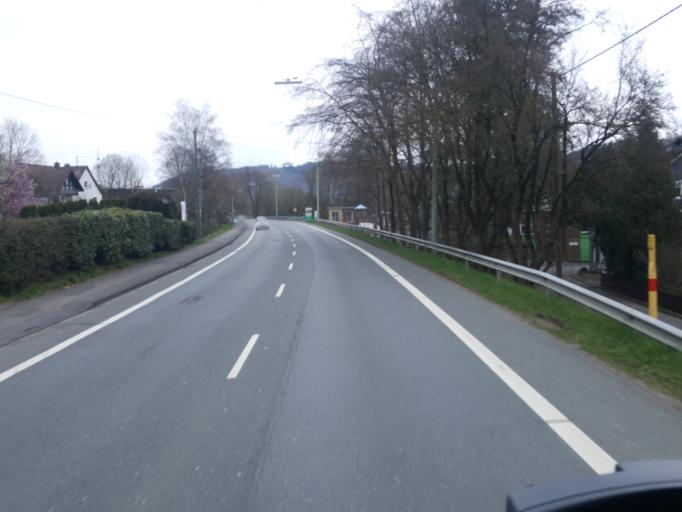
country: DE
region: North Rhine-Westphalia
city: Kreuztal
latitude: 50.9589
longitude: 8.0239
